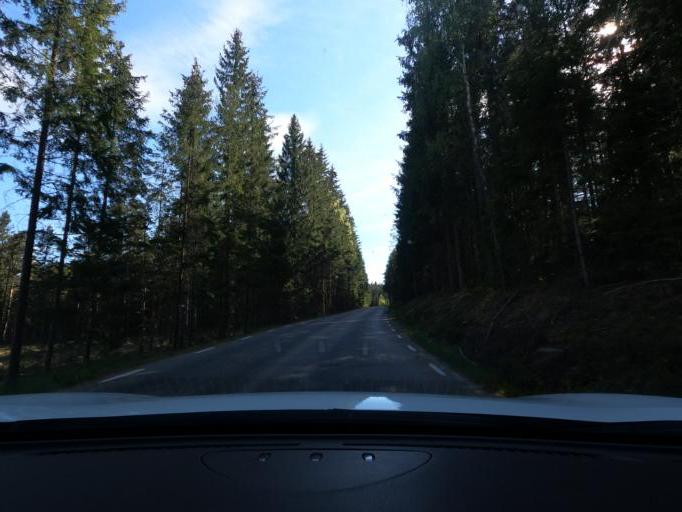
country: SE
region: Vaestra Goetaland
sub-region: Harryda Kommun
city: Hindas
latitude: 57.6363
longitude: 12.3370
